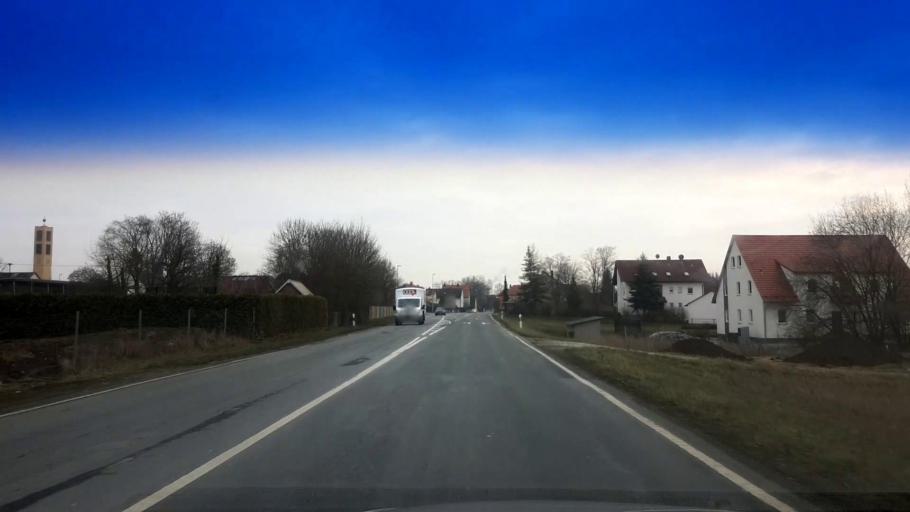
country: DE
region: Bavaria
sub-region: Upper Franconia
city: Altendorf
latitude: 49.8010
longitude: 11.0088
